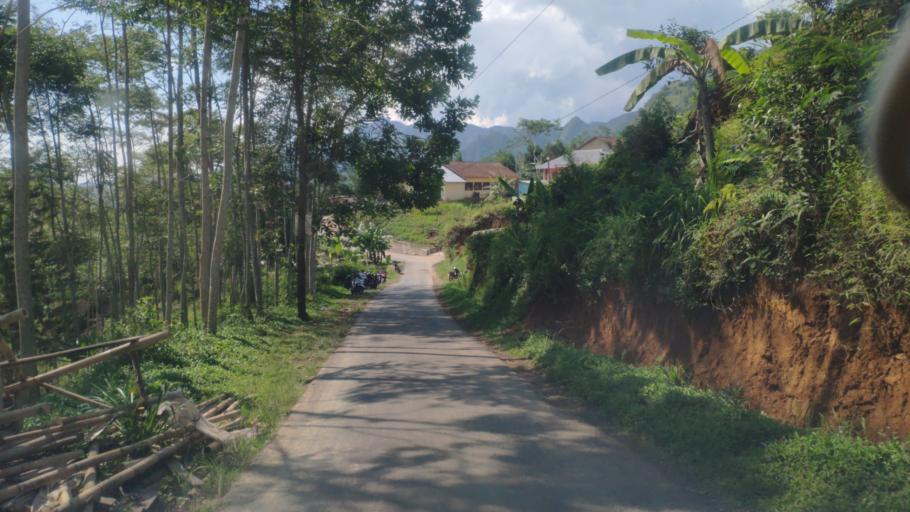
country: ID
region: Central Java
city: Buaran
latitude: -7.2382
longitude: 109.6194
